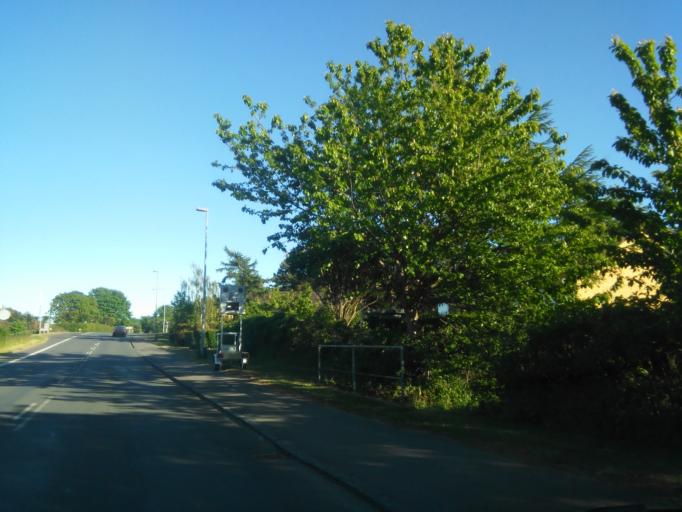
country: DK
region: Capital Region
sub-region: Bornholm Kommune
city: Ronne
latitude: 55.2702
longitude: 14.8019
